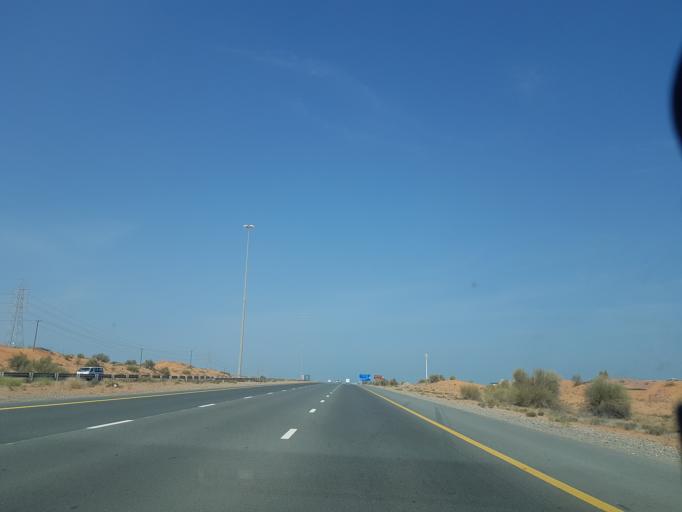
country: AE
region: Ra's al Khaymah
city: Ras al-Khaimah
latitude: 25.6896
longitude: 55.8801
